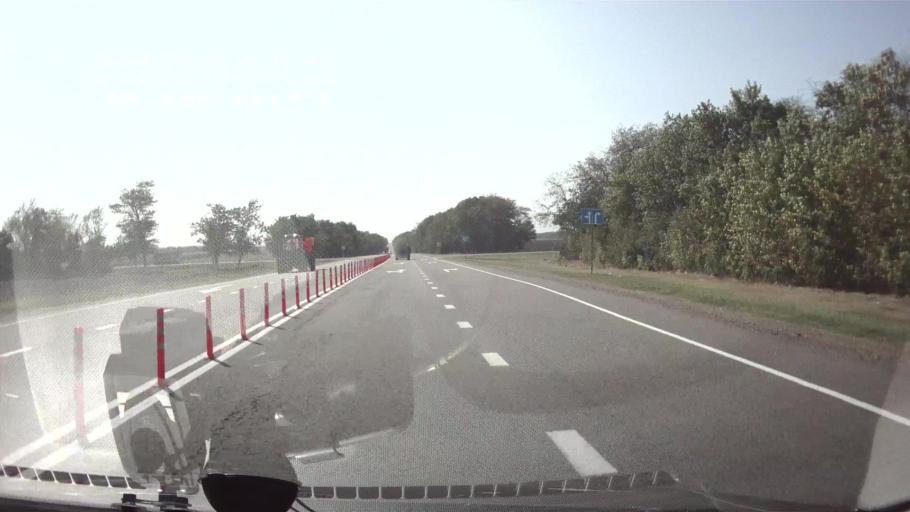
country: RU
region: Krasnodarskiy
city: Novopokrovskaya
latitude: 45.8187
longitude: 40.7201
